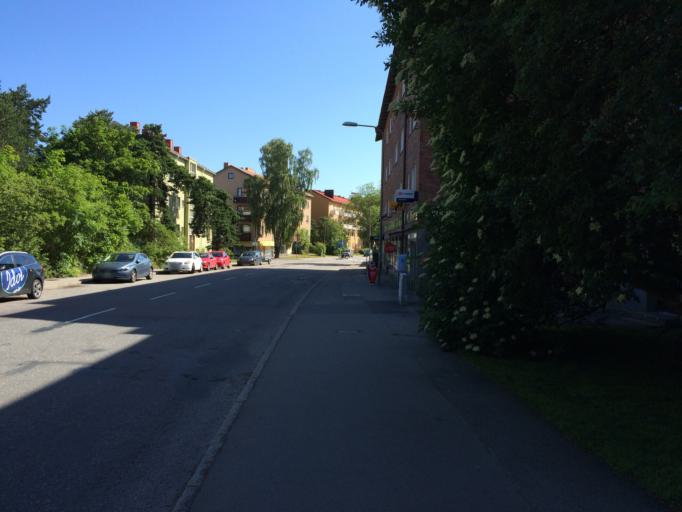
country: SE
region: Stockholm
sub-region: Stockholms Kommun
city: Bromma
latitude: 59.3009
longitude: 17.9844
